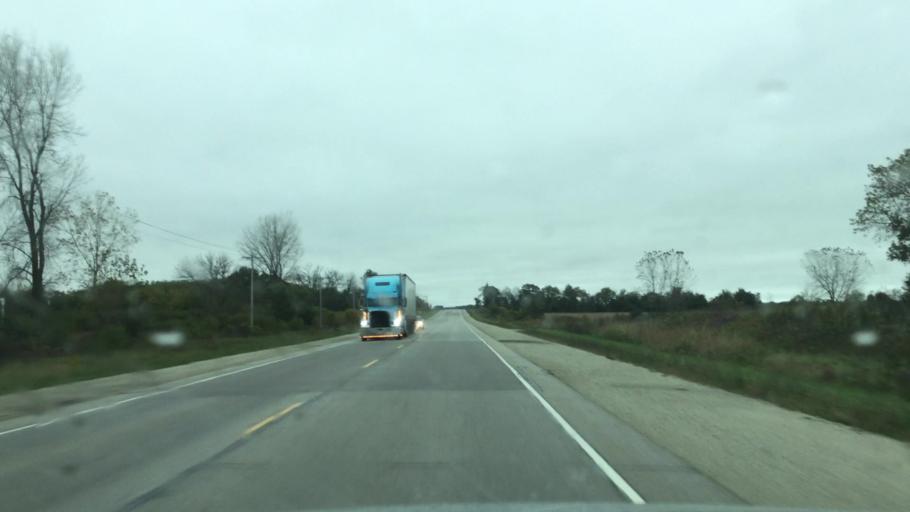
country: US
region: Wisconsin
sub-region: Racine County
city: Union Grove
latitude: 42.7328
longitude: -87.9985
